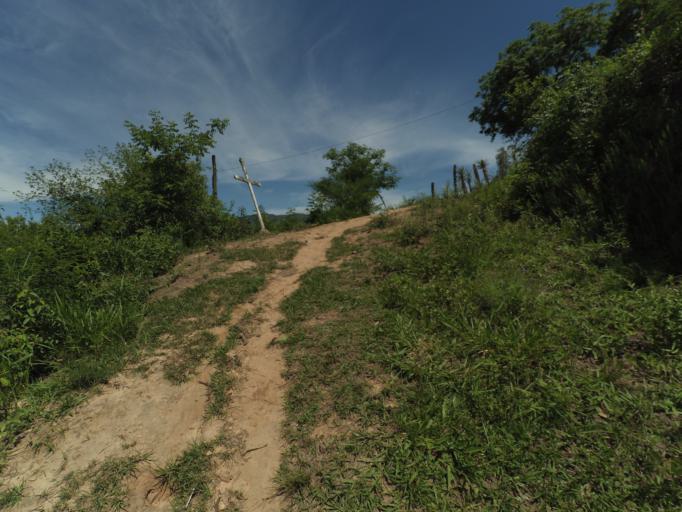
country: BO
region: Chuquisaca
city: Monteagudo
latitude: -19.8028
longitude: -63.9533
